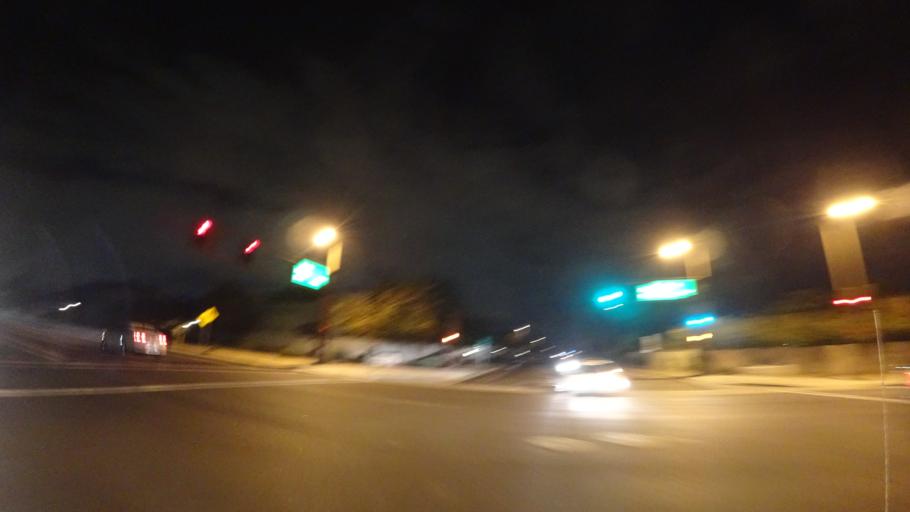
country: US
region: Arizona
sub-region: Maricopa County
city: Guadalupe
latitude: 33.3636
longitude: -111.9546
